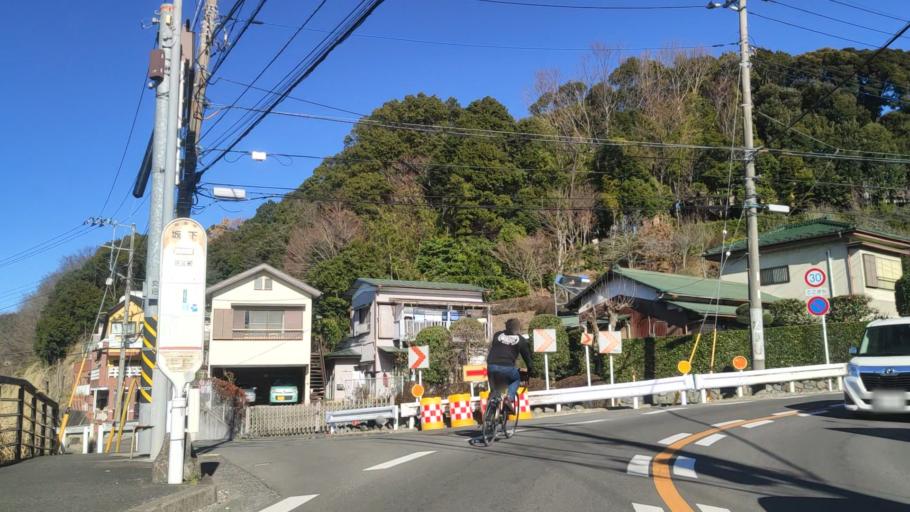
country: JP
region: Kanagawa
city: Minami-rinkan
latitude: 35.5101
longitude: 139.5211
